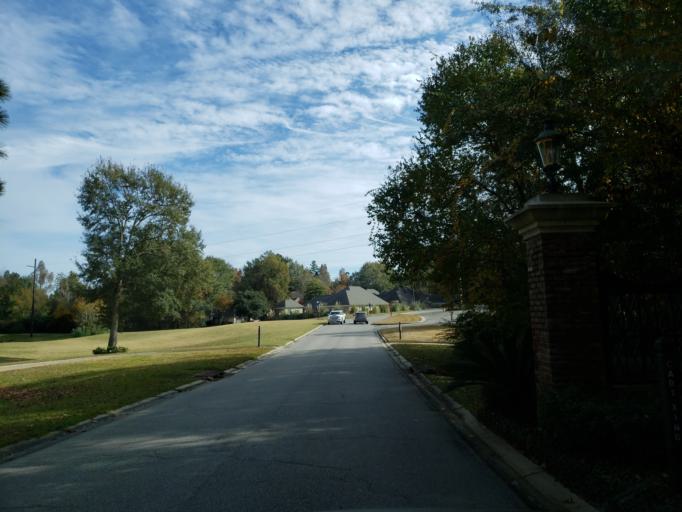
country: US
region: Mississippi
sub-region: Lamar County
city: West Hattiesburg
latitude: 31.3162
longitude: -89.4694
